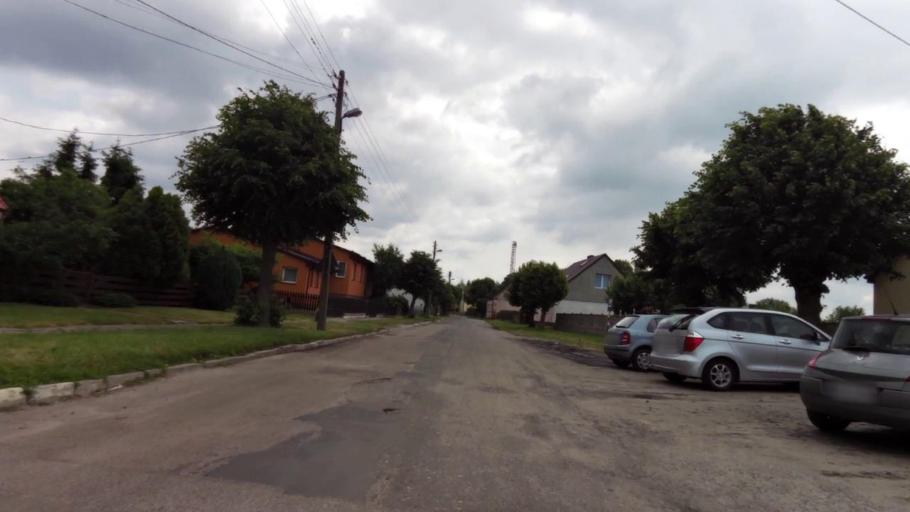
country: PL
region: West Pomeranian Voivodeship
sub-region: Powiat goleniowski
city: Goleniow
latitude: 53.5041
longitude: 14.7027
